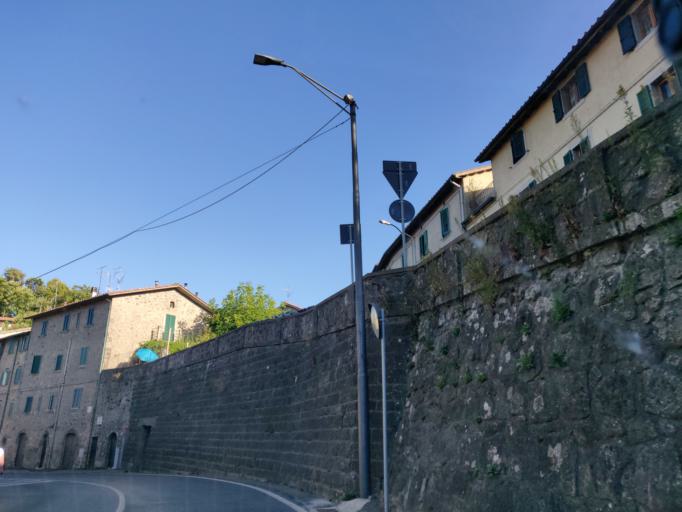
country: IT
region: Tuscany
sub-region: Provincia di Siena
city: Abbadia San Salvatore
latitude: 42.8774
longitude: 11.6791
